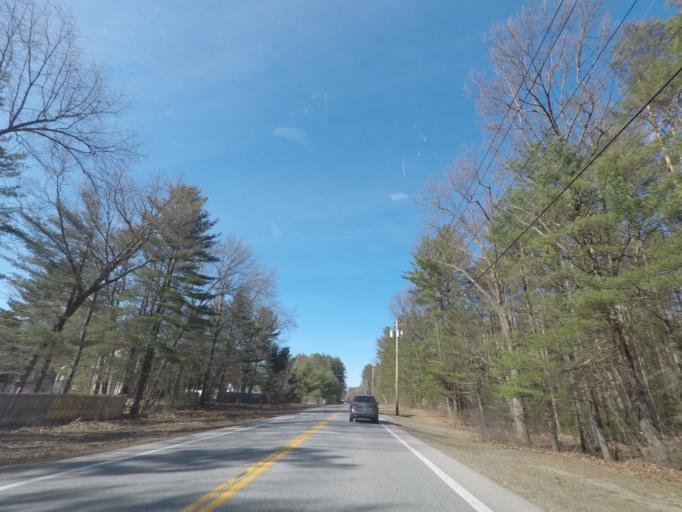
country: US
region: New York
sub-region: Saratoga County
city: Milton
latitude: 43.0278
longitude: -73.8479
